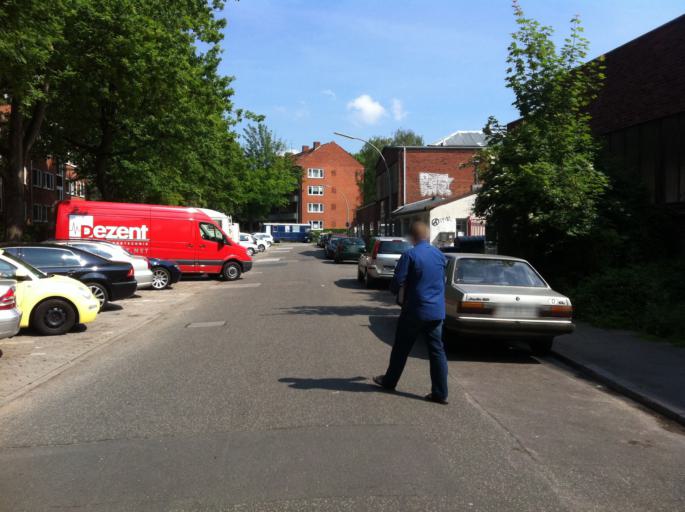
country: DE
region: Hamburg
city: Altona
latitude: 53.5546
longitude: 9.9451
